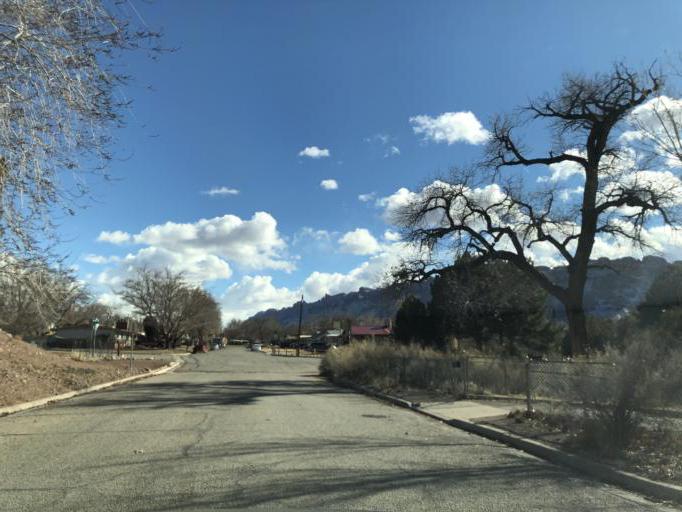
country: US
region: Utah
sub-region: Grand County
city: Moab
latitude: 38.5708
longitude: -109.5381
